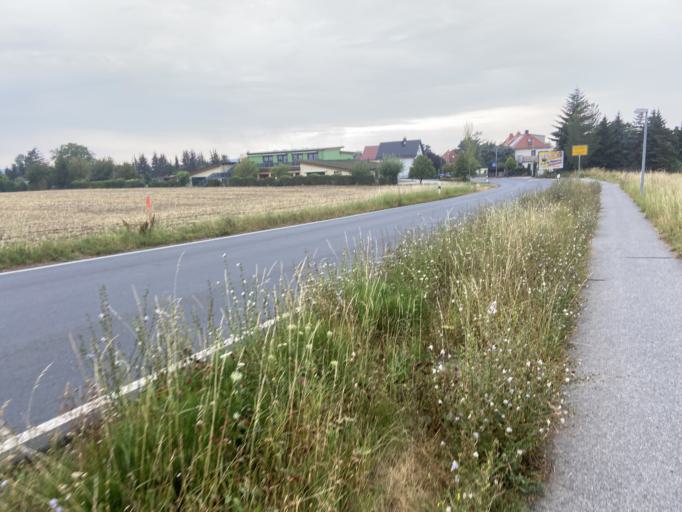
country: DE
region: Saxony
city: Tharandt
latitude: 51.0180
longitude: 13.5803
